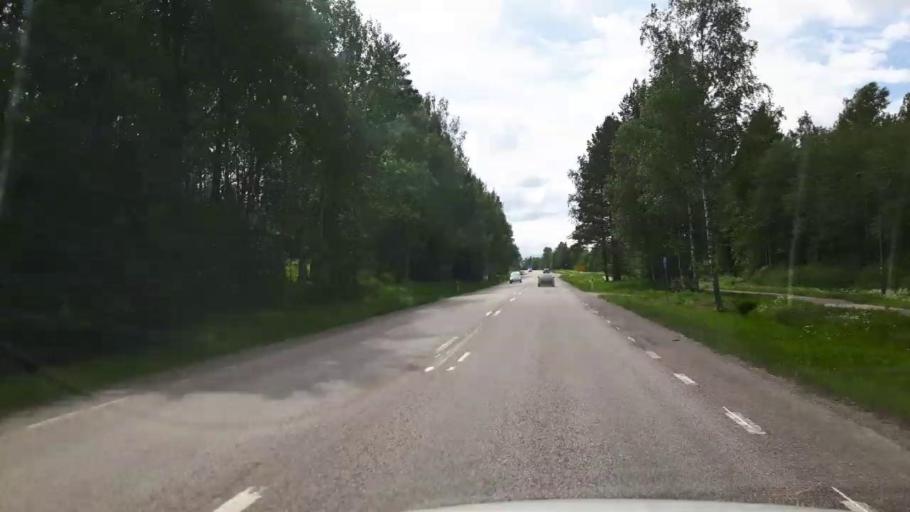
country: SE
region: Vaestmanland
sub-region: Fagersta Kommun
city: Fagersta
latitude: 59.9694
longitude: 15.7741
